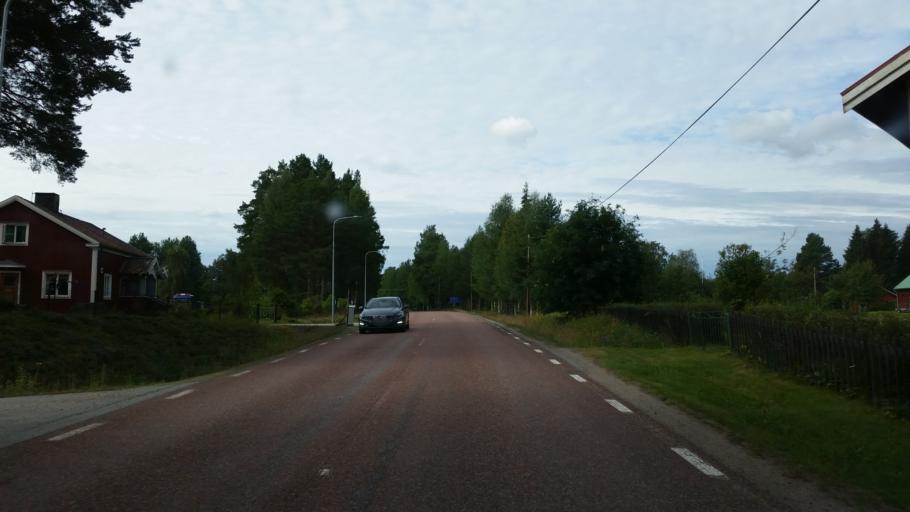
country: SE
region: Vaesternorrland
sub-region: Ange Kommun
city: Ange
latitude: 62.1871
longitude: 15.6566
